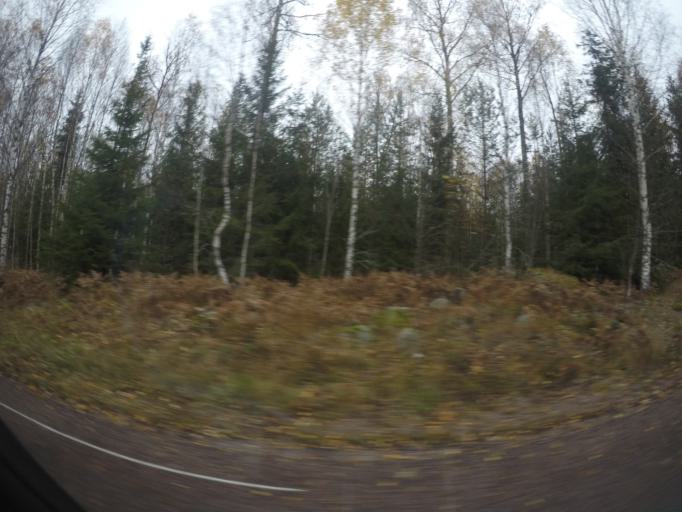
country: SE
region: Vaestmanland
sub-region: Surahammars Kommun
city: Surahammar
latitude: 59.6706
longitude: 16.0782
